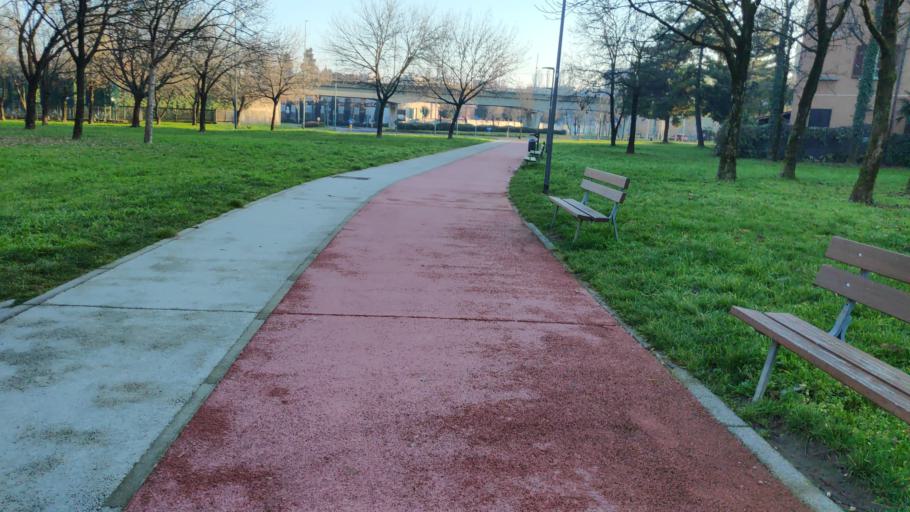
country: IT
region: Lombardy
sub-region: Citta metropolitana di Milano
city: Cologno Monzese
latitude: 45.5291
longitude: 9.2829
